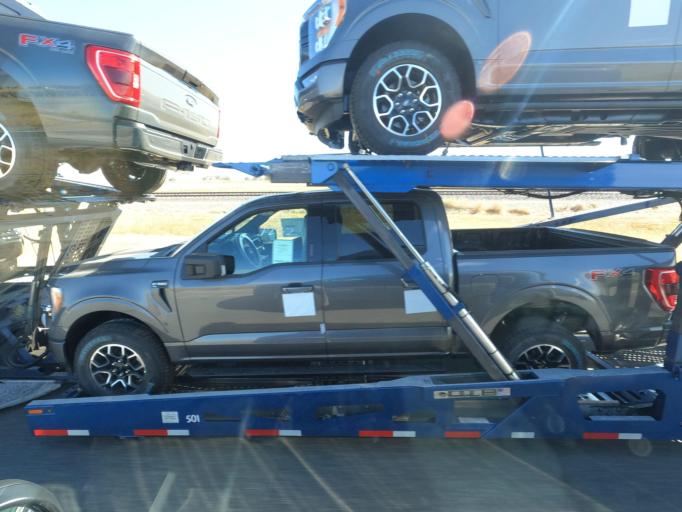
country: US
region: Colorado
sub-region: Weld County
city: Lochbuie
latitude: 40.0246
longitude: -104.6896
